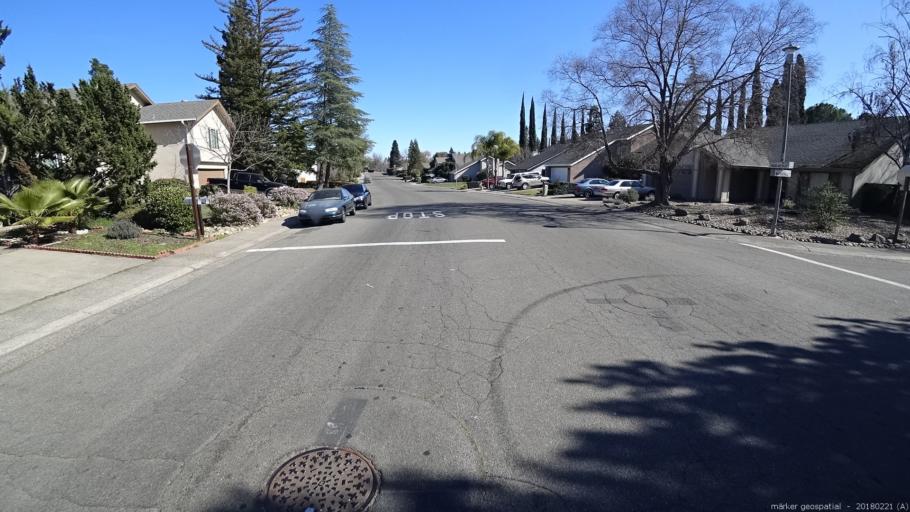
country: US
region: California
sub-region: Sacramento County
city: Citrus Heights
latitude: 38.6838
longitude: -121.2604
